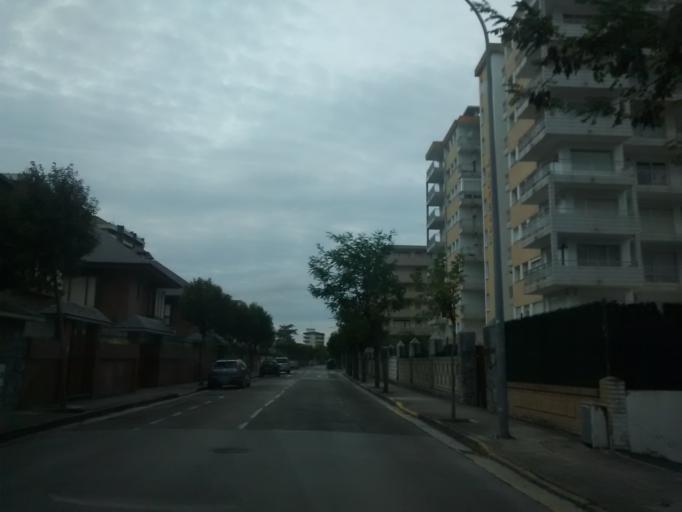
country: ES
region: Cantabria
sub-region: Provincia de Cantabria
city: Laredo
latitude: 43.4117
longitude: -3.4333
